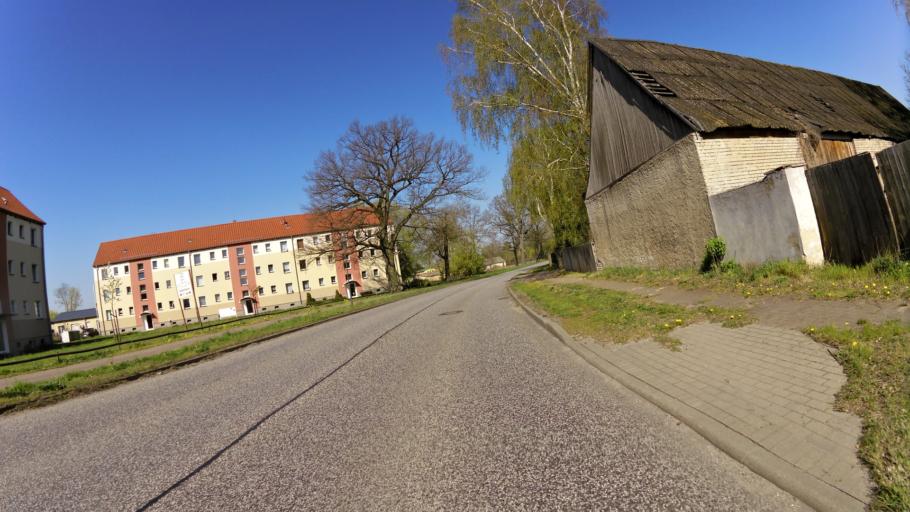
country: DE
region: Brandenburg
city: Pessin
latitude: 52.6428
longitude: 12.6663
